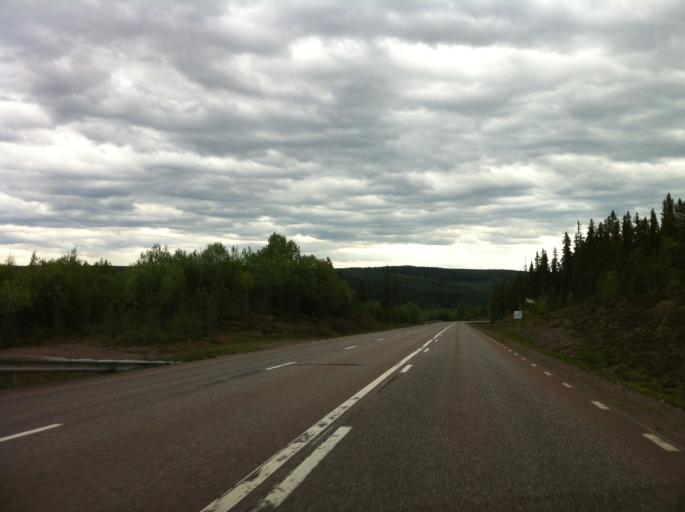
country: SE
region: Dalarna
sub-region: Malung-Saelens kommun
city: Malung
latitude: 61.1591
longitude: 13.2376
